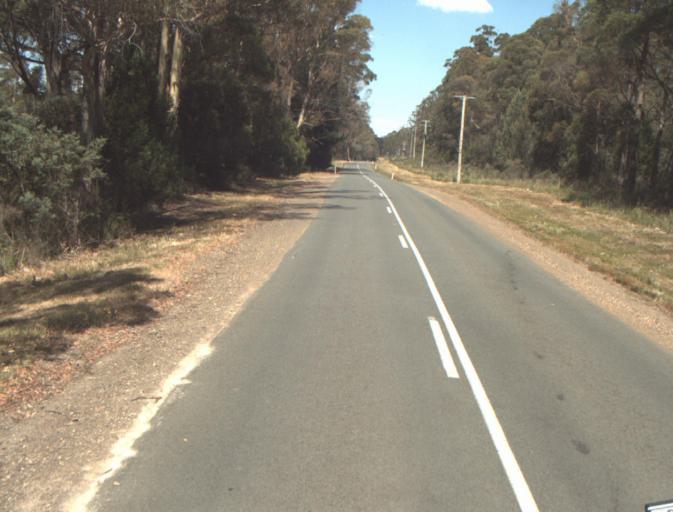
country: AU
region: Tasmania
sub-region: Launceston
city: Mayfield
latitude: -41.2857
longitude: 147.1269
